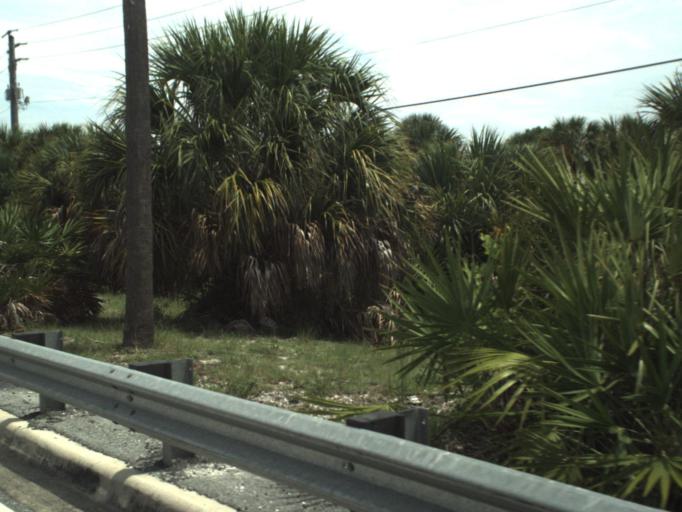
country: US
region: Florida
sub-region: Palm Beach County
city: Jupiter
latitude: 26.9497
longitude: -80.0851
